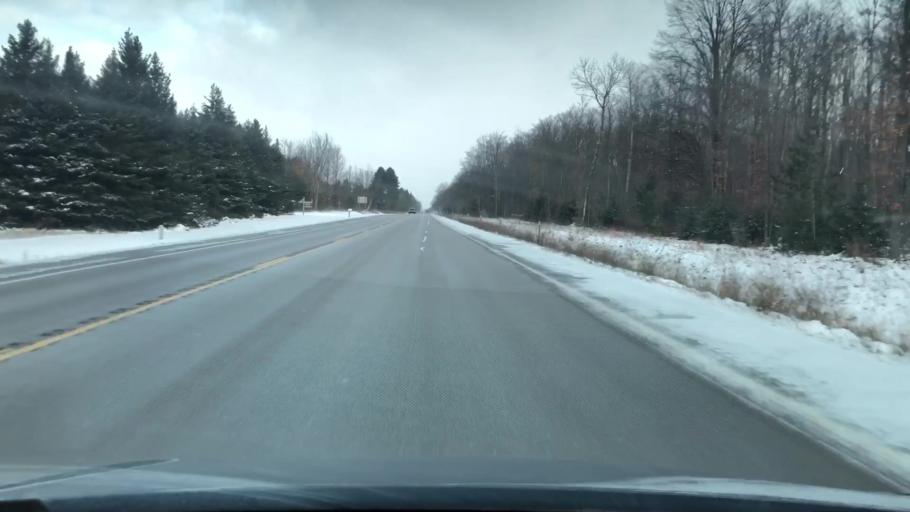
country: US
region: Michigan
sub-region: Grand Traverse County
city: Kingsley
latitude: 44.4600
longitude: -85.6976
